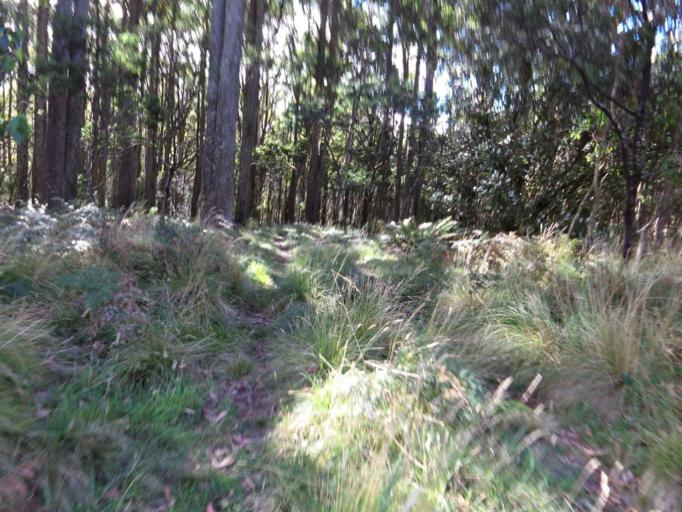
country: AU
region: Victoria
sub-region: Hume
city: Sunbury
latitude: -37.3738
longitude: 144.6150
